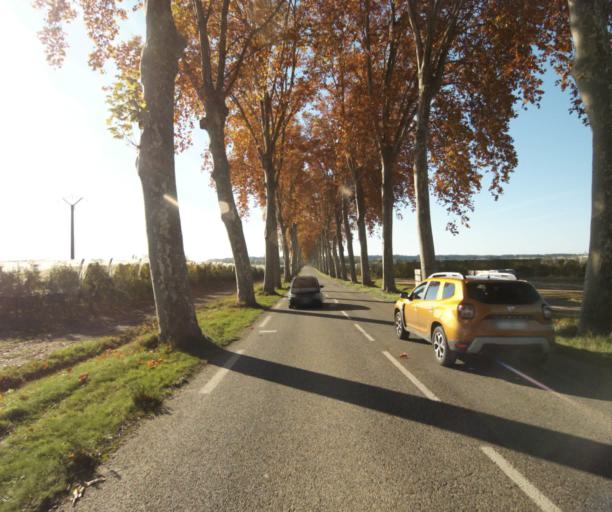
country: FR
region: Midi-Pyrenees
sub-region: Departement du Tarn-et-Garonne
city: Montech
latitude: 43.9542
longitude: 1.2019
